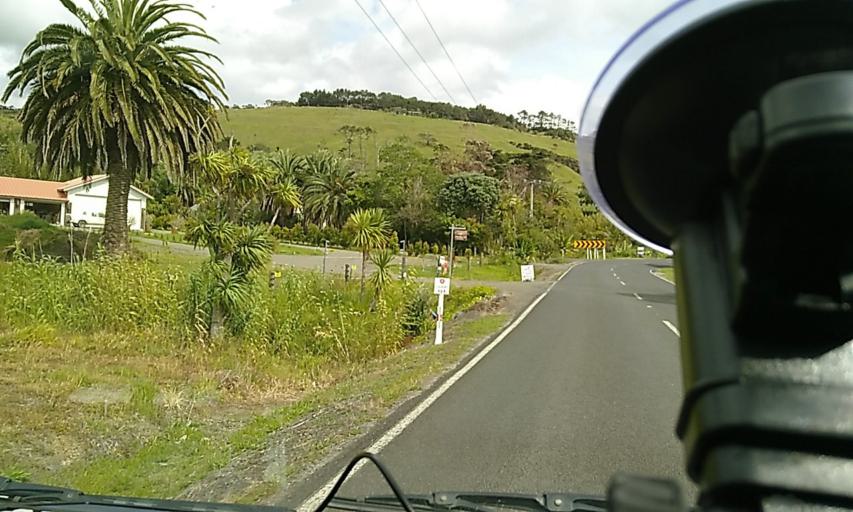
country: NZ
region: Northland
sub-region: Far North District
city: Ahipara
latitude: -35.5306
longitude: 173.3899
